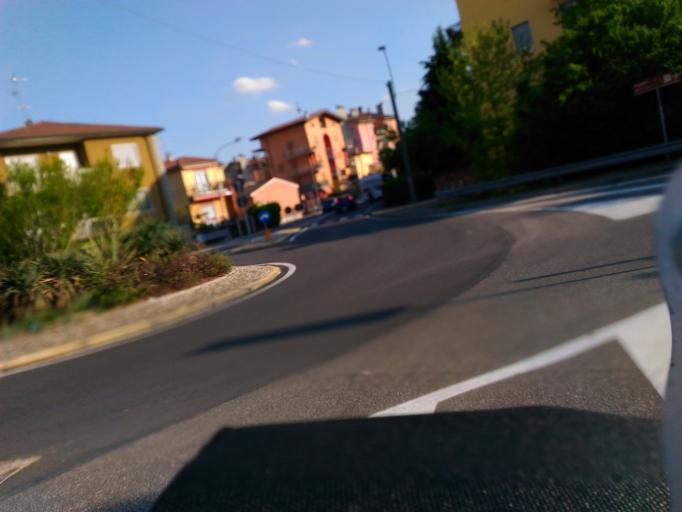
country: IT
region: Lombardy
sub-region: Provincia di Lodi
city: Lodi
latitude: 45.3170
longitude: 9.4902
